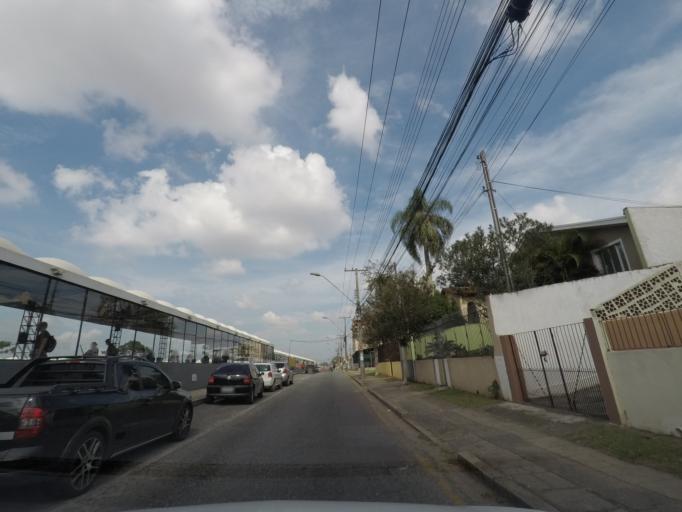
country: BR
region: Parana
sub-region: Pinhais
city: Pinhais
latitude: -25.4511
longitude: -49.2154
